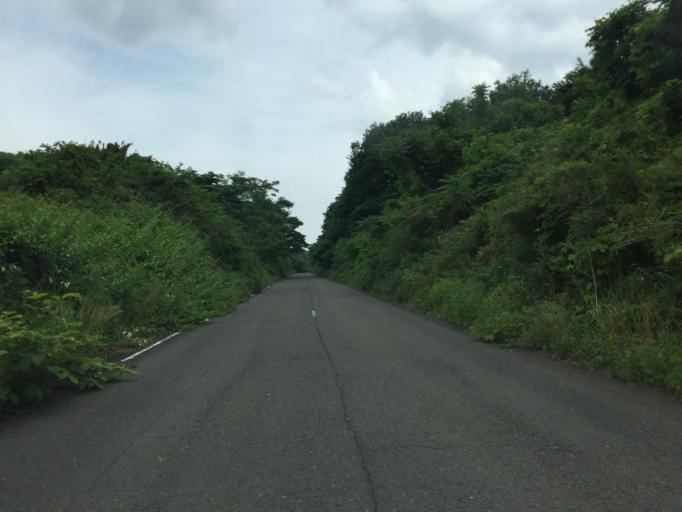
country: JP
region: Miyagi
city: Marumori
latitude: 37.8747
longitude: 140.8346
